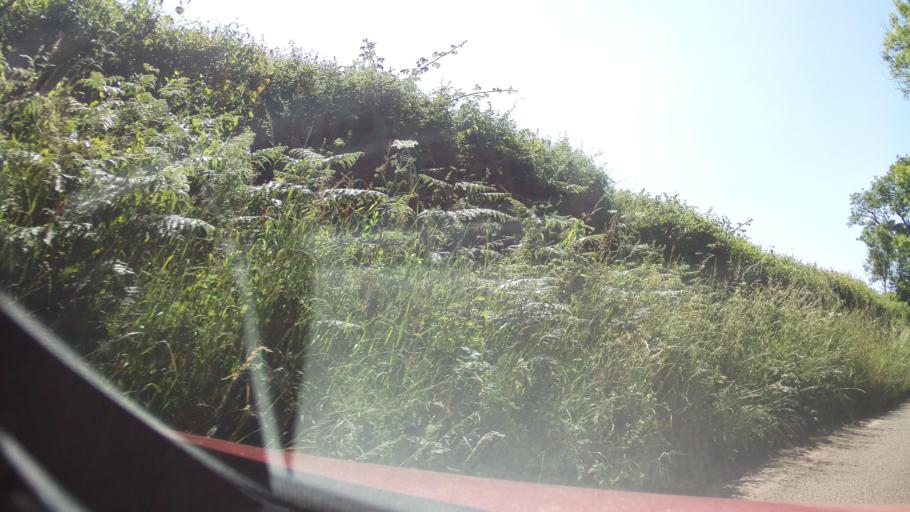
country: GB
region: England
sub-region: Borough of Torbay
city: Paignton
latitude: 50.4143
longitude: -3.5959
